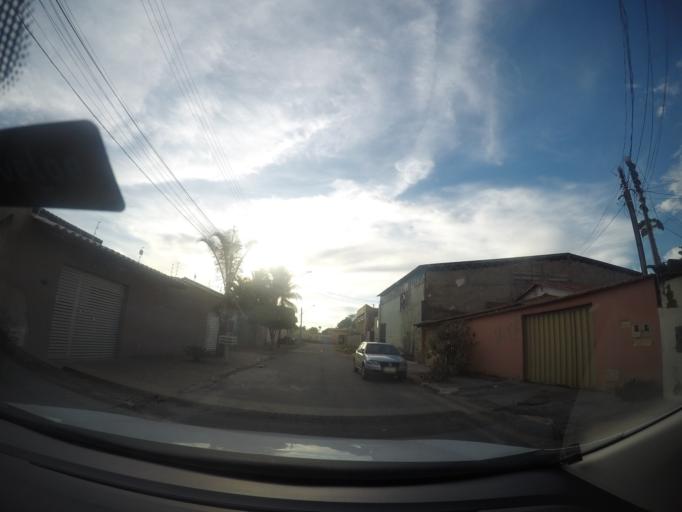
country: BR
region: Goias
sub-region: Goiania
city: Goiania
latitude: -16.6843
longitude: -49.3184
